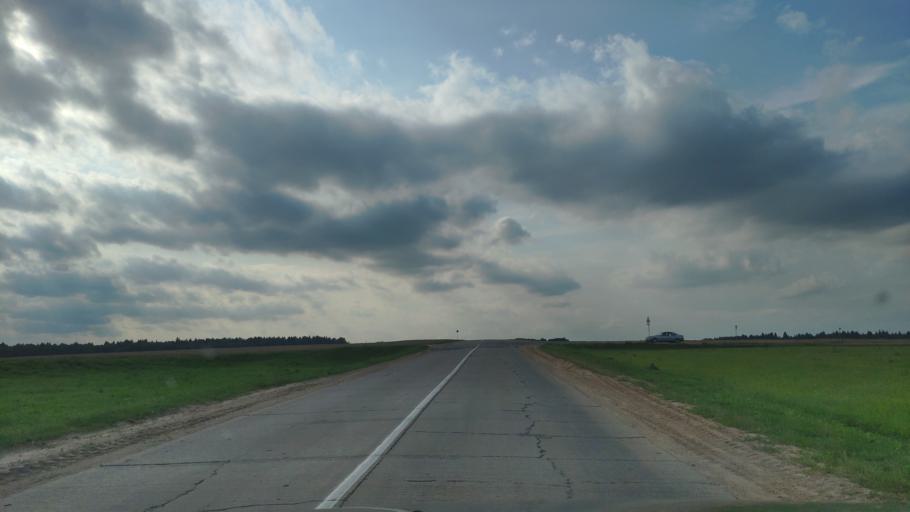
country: BY
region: Minsk
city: Khatsyezhyna
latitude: 53.8325
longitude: 27.3056
